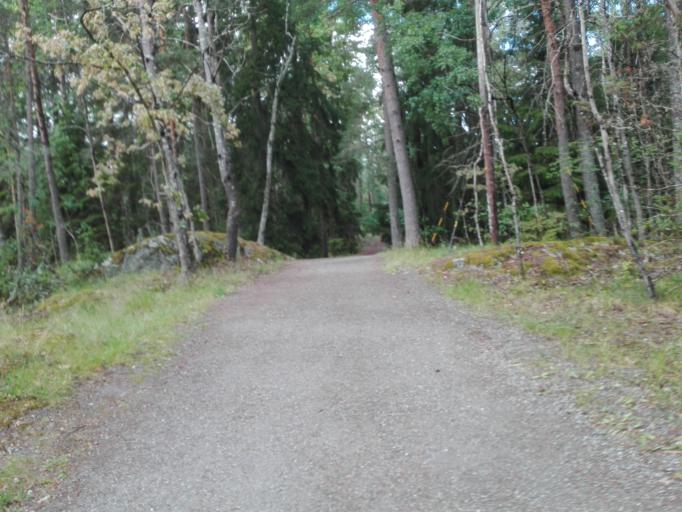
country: SE
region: Stockholm
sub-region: Nacka Kommun
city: Fisksatra
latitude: 59.2853
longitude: 18.2629
